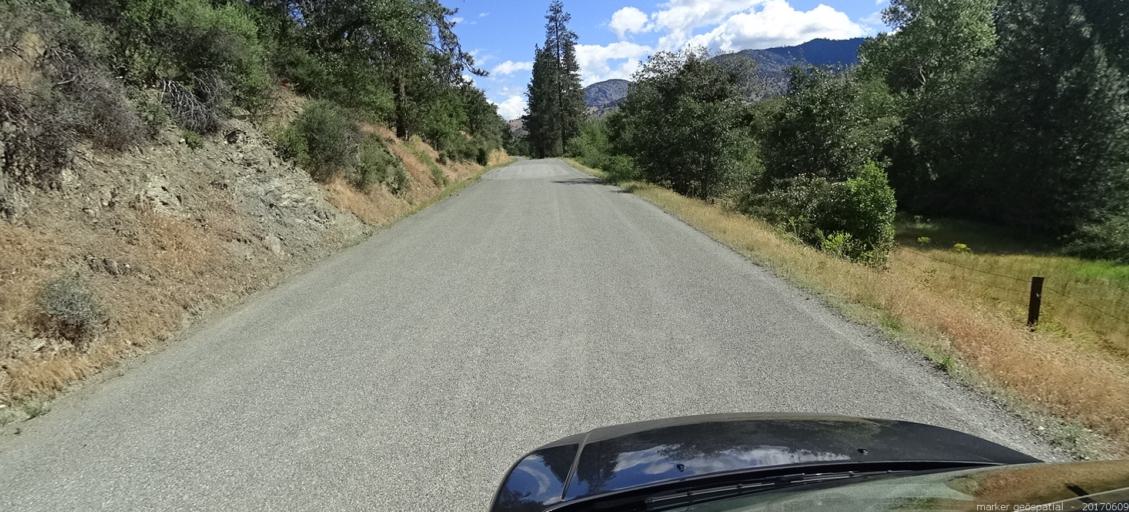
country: US
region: California
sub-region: Siskiyou County
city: Yreka
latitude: 41.3355
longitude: -122.8289
